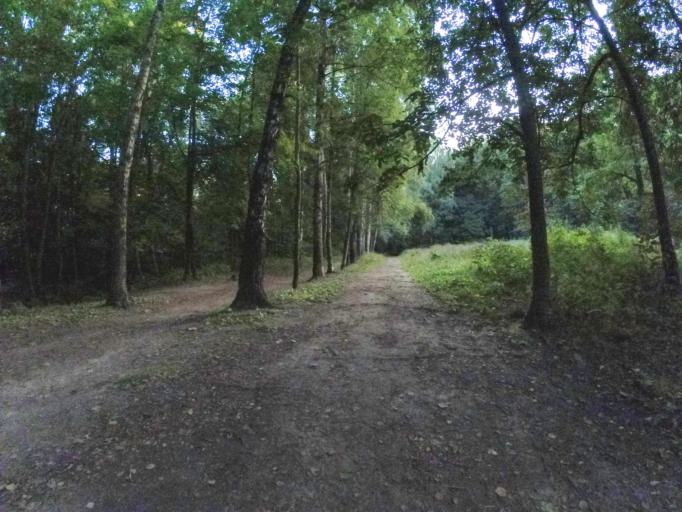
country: RU
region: Moscow
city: Strogino
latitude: 55.8473
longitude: 37.3986
